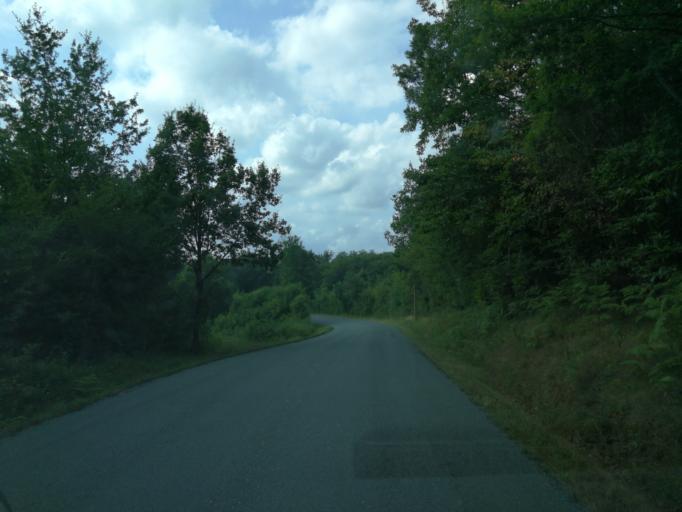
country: FR
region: Aquitaine
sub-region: Departement du Lot-et-Garonne
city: Monsempron-Libos
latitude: 44.5392
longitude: 0.9215
